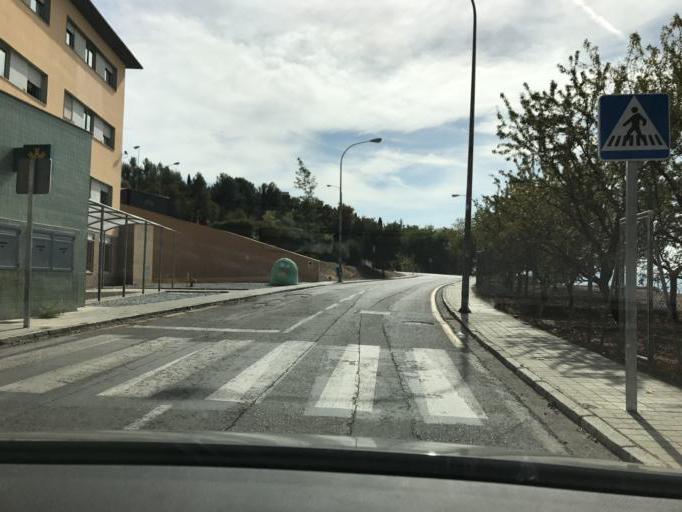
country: ES
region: Andalusia
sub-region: Provincia de Granada
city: Granada
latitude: 37.1922
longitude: -3.5981
